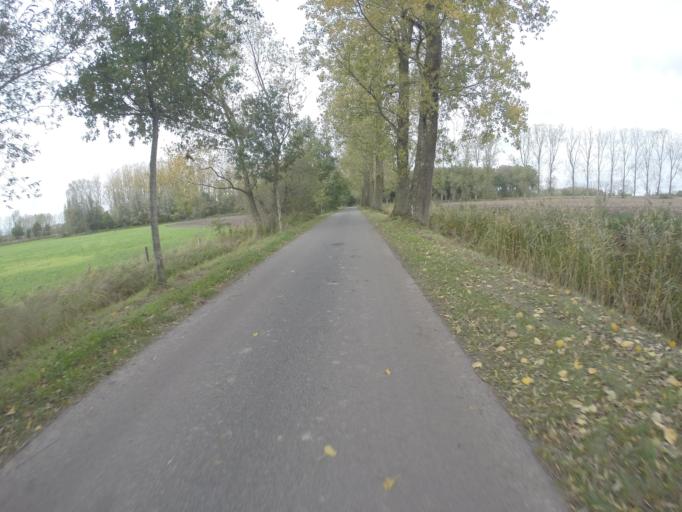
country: BE
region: Flanders
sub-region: Provincie Oost-Vlaanderen
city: Knesselare
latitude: 51.1686
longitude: 3.4265
